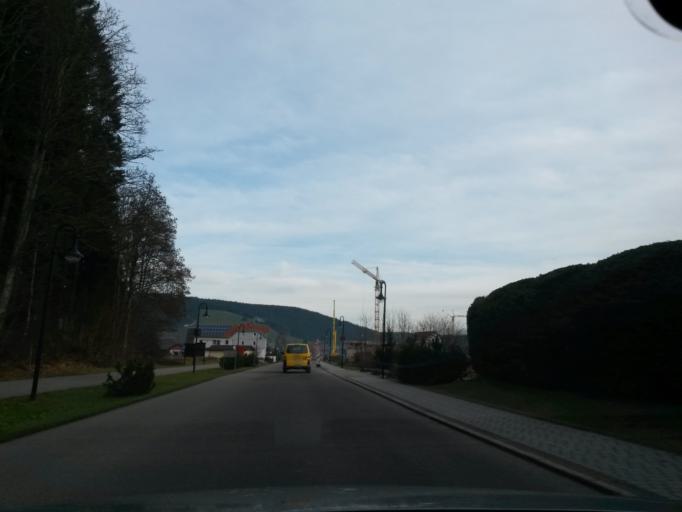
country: DE
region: Baden-Wuerttemberg
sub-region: Freiburg Region
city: Titisee-Neustadt
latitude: 47.9051
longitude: 8.1567
